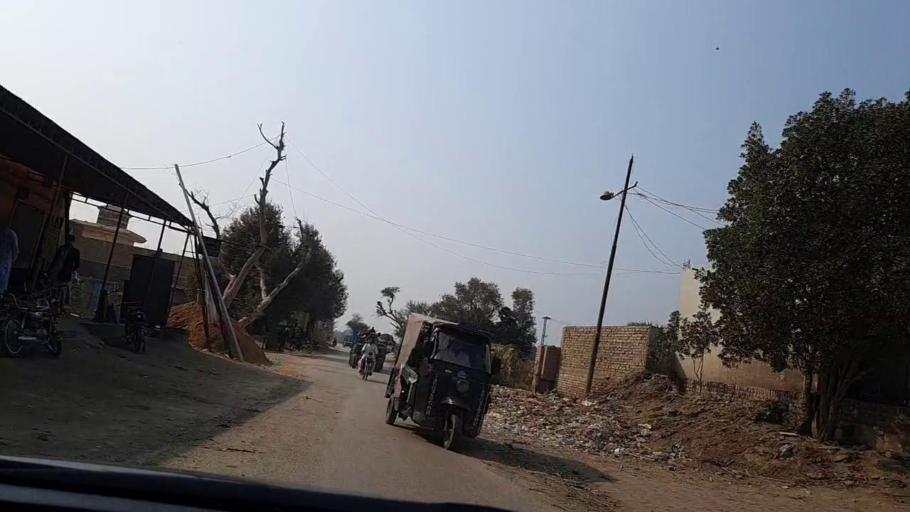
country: PK
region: Sindh
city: Sakrand
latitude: 26.1383
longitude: 68.2593
